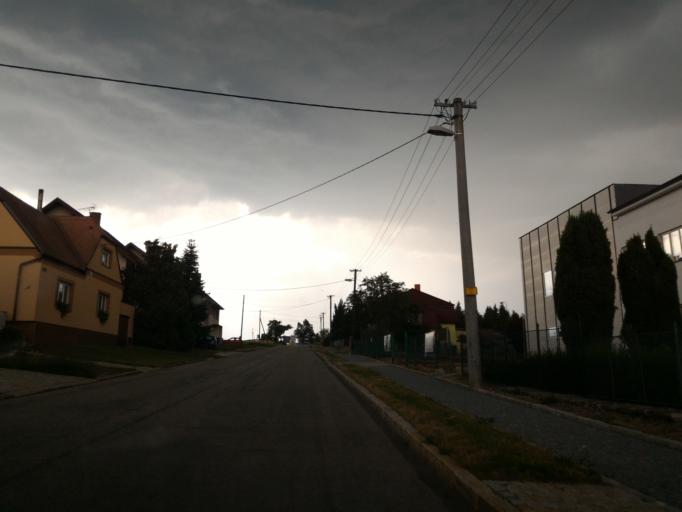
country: CZ
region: Vysocina
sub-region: Okres Jihlava
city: Telc
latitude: 49.1419
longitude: 15.5586
